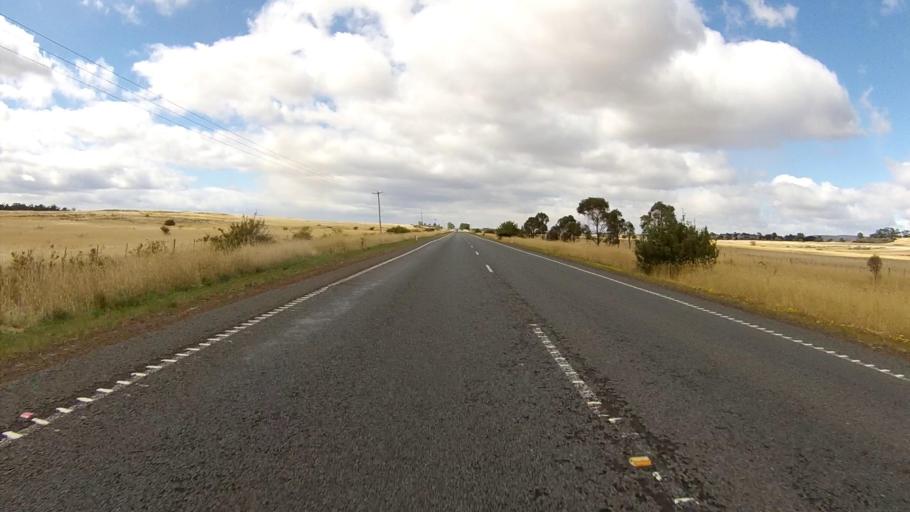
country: AU
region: Tasmania
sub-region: Northern Midlands
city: Evandale
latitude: -41.8543
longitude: 147.4527
